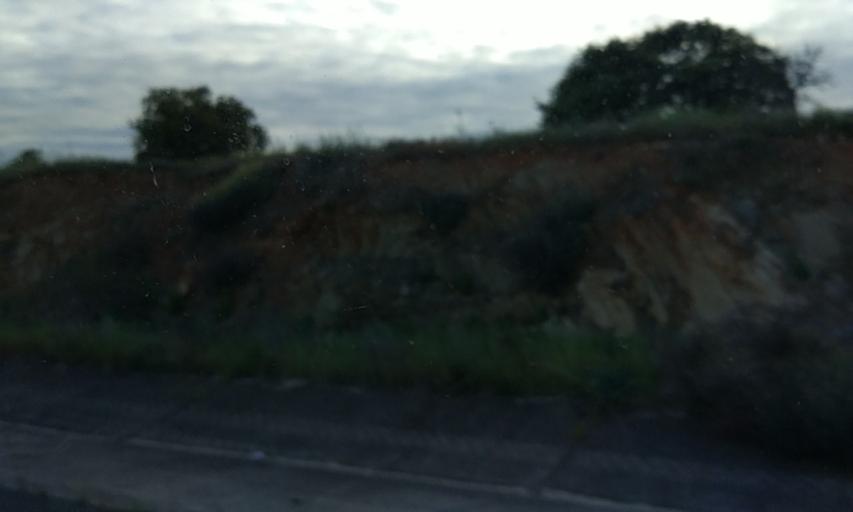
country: ES
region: Extremadura
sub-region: Provincia de Caceres
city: Santiago del Campo
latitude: 39.6368
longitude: -6.3934
